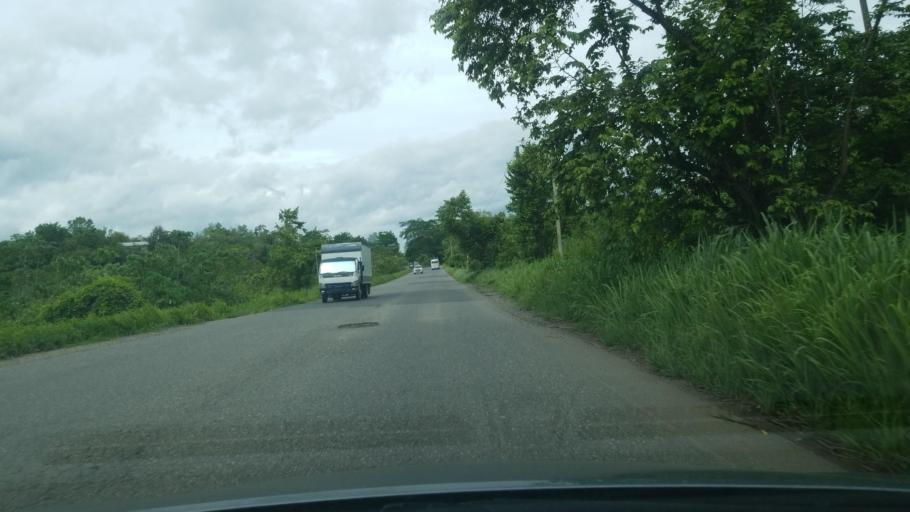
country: HN
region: Santa Barbara
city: La Flecha
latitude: 15.3008
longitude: -88.4556
